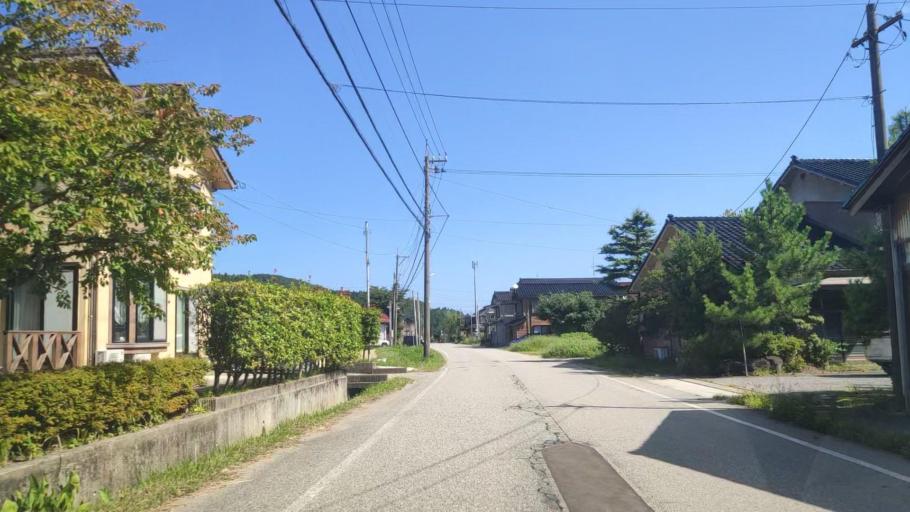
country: JP
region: Ishikawa
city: Nanao
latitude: 37.3771
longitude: 136.8780
